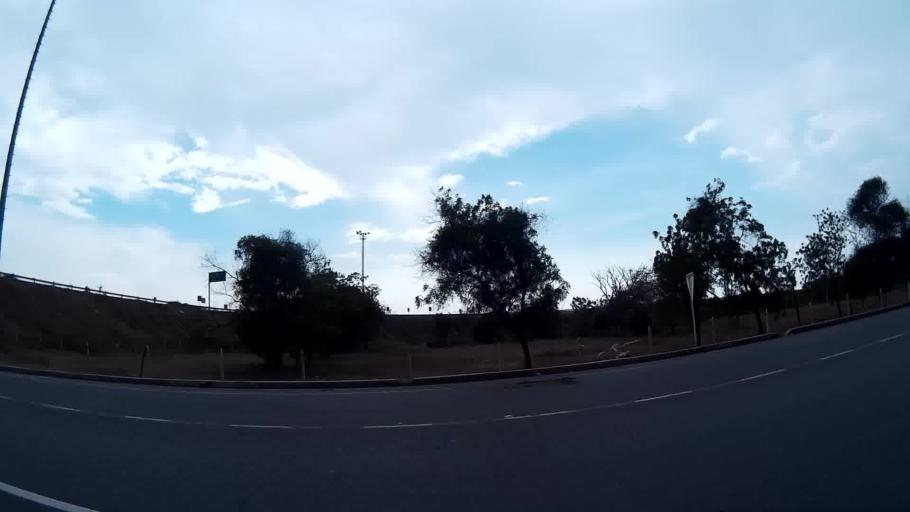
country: CO
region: Magdalena
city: Cienaga
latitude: 11.0056
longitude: -74.2173
